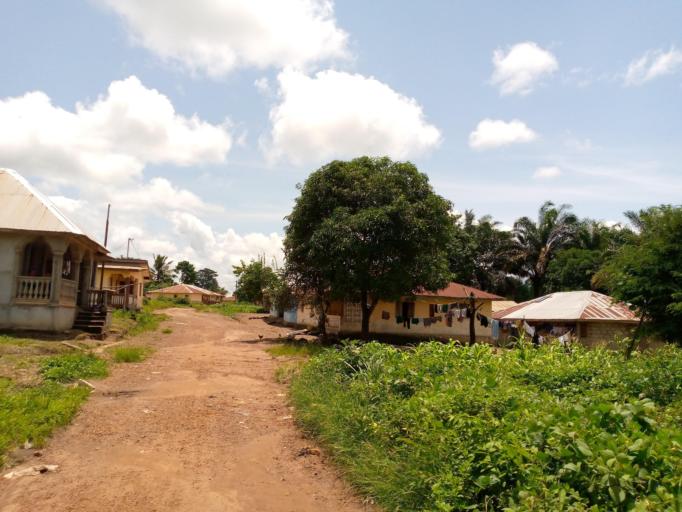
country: SL
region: Northern Province
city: Magburaka
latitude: 8.7171
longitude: -11.9606
